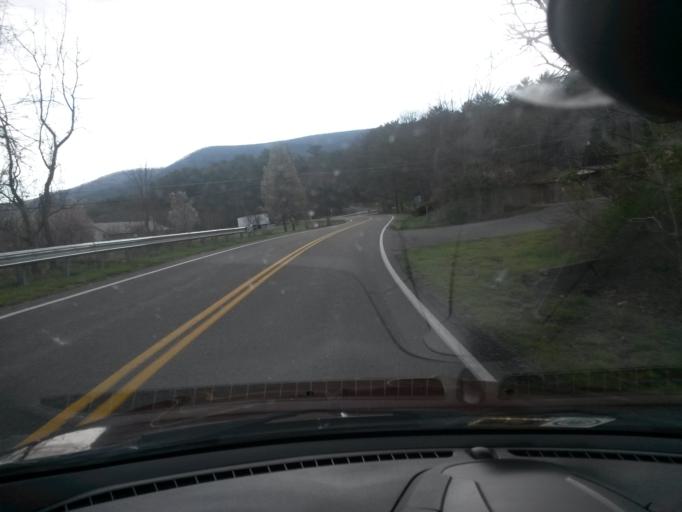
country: US
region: Virginia
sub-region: Alleghany County
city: Clifton Forge
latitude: 37.8103
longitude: -79.6822
